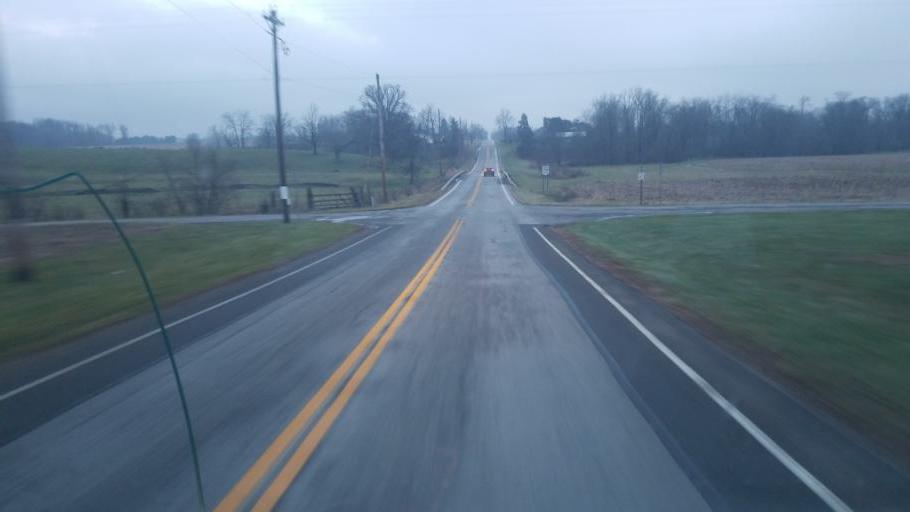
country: US
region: Ohio
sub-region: Wyandot County
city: Upper Sandusky
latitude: 40.8919
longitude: -83.1317
